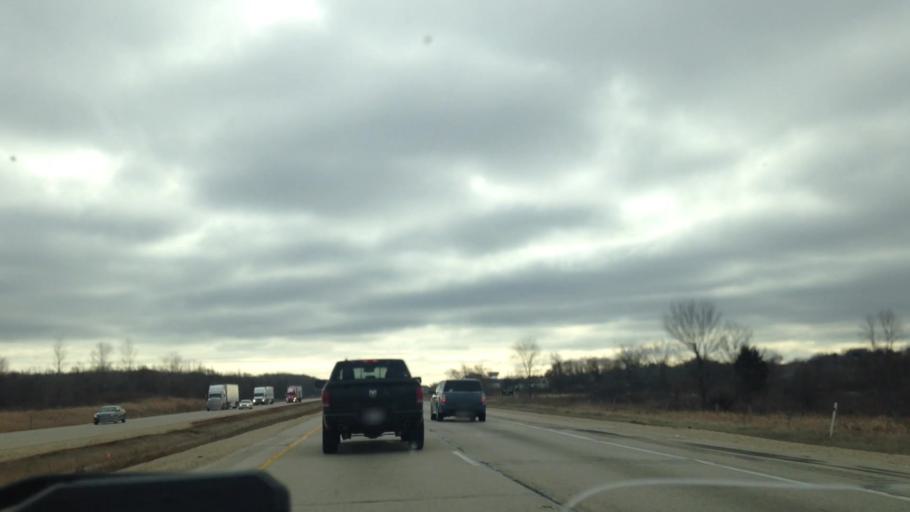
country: US
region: Wisconsin
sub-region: Washington County
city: Slinger
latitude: 43.3873
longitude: -88.3102
